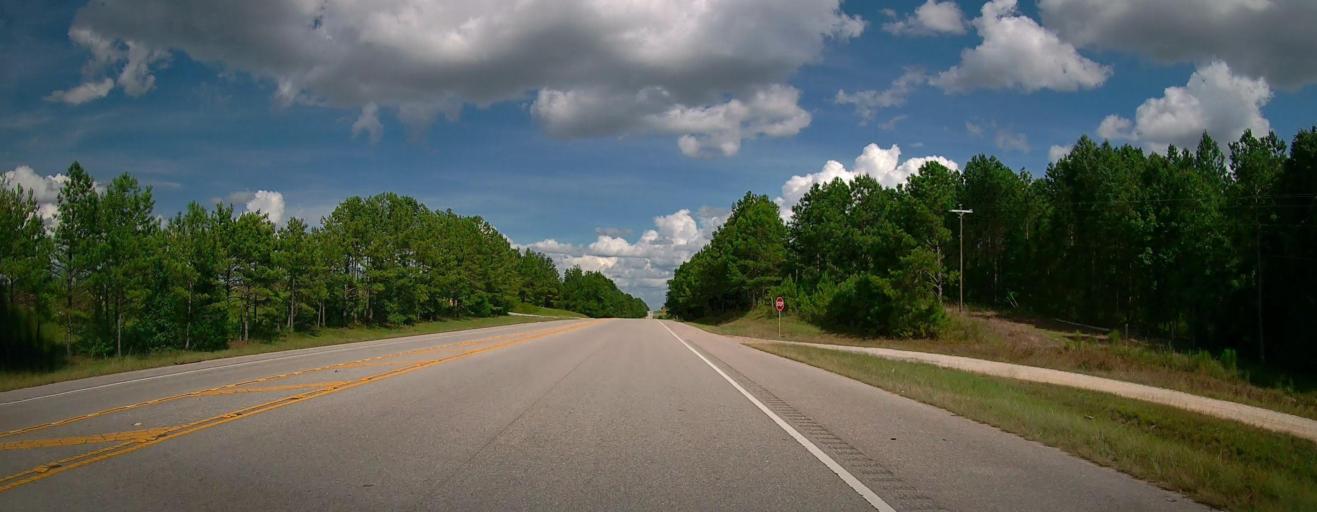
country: US
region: Alabama
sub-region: Macon County
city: Tuskegee
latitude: 32.4674
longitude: -85.5742
